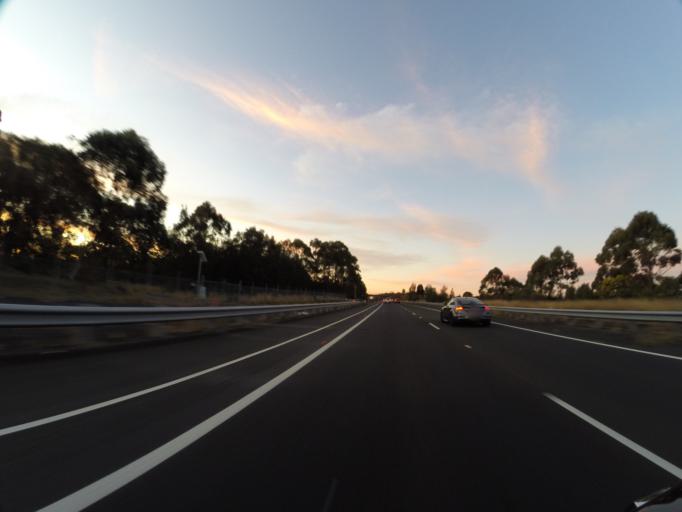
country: AU
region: New South Wales
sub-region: Wollongong
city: Helensburgh
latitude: -34.1511
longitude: 150.9896
